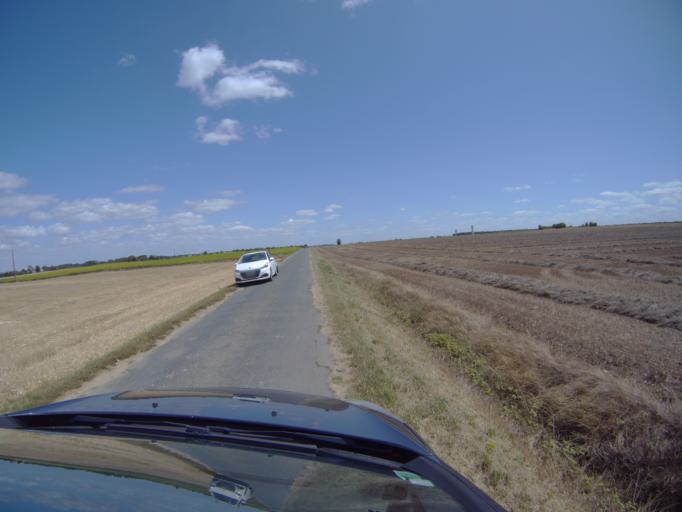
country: FR
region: Poitou-Charentes
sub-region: Departement de la Charente-Maritime
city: Courcon
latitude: 46.2473
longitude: -0.8015
